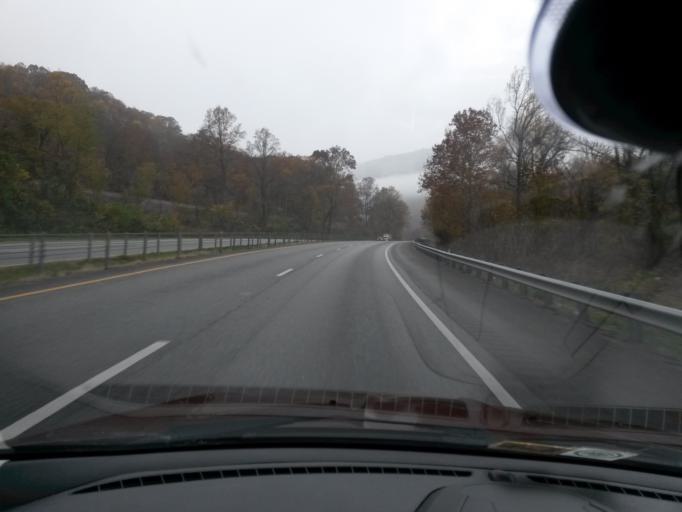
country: US
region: Virginia
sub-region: City of Covington
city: Fairlawn
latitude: 37.7780
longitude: -79.9188
